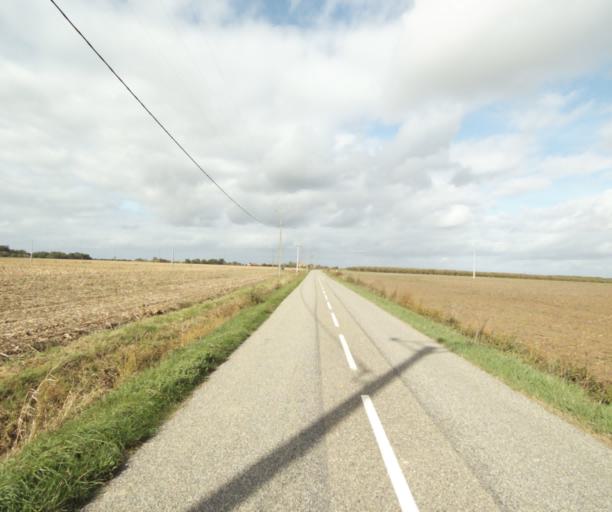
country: FR
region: Midi-Pyrenees
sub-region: Departement du Tarn-et-Garonne
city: Finhan
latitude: 43.9059
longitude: 1.1468
